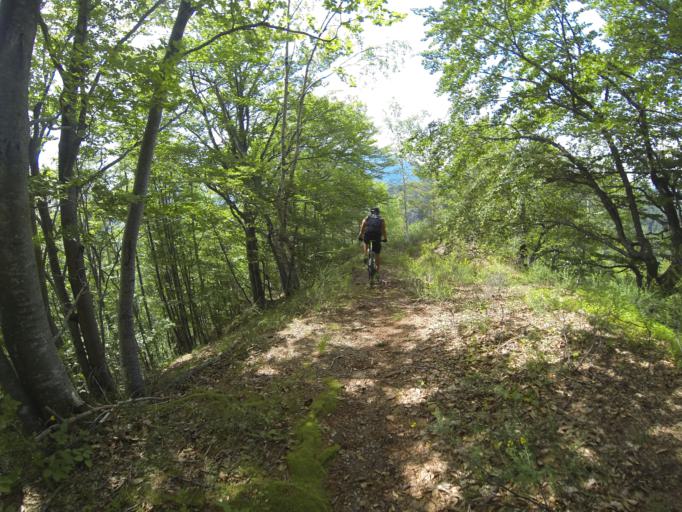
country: RO
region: Valcea
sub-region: Oras Baile Olanesti
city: Cheia
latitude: 45.2329
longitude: 24.1742
